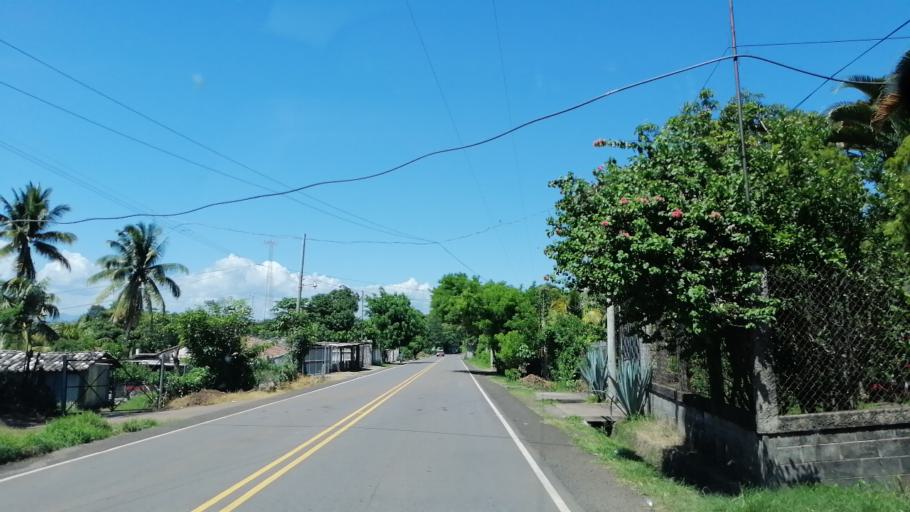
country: SV
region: San Miguel
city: Ciudad Barrios
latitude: 13.8140
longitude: -88.1757
